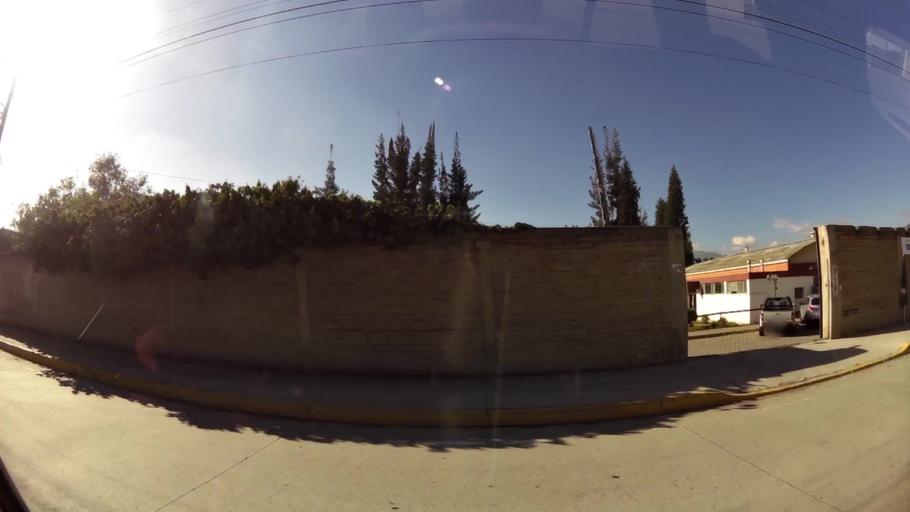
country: EC
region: Chimborazo
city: Riobamba
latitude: -1.6461
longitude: -78.6790
